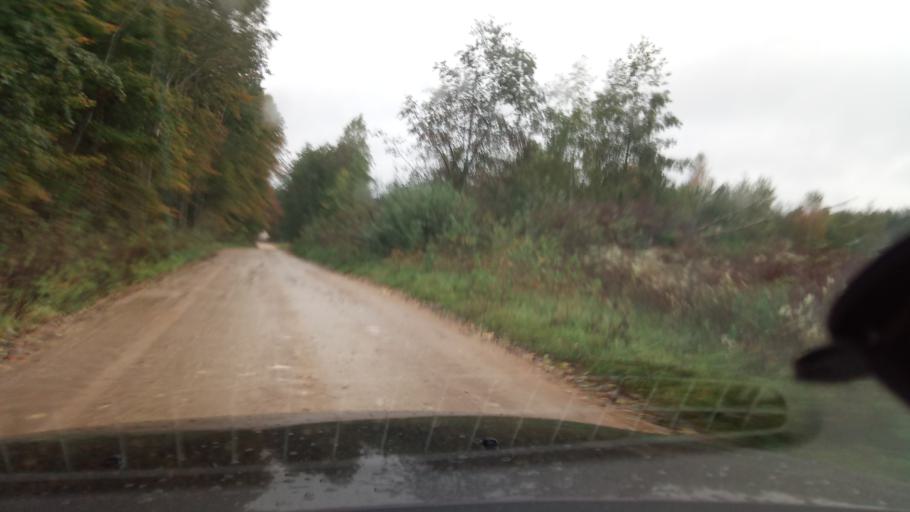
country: LT
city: Skaidiskes
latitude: 54.5574
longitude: 25.4915
